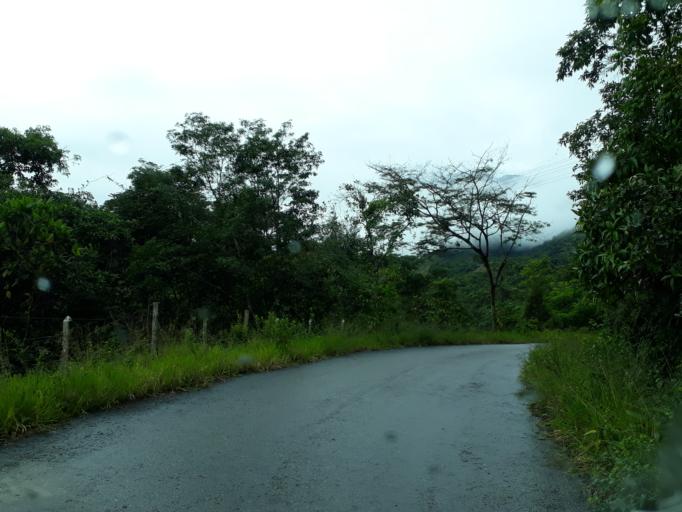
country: CO
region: Cundinamarca
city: Medina
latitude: 4.6754
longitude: -73.3232
